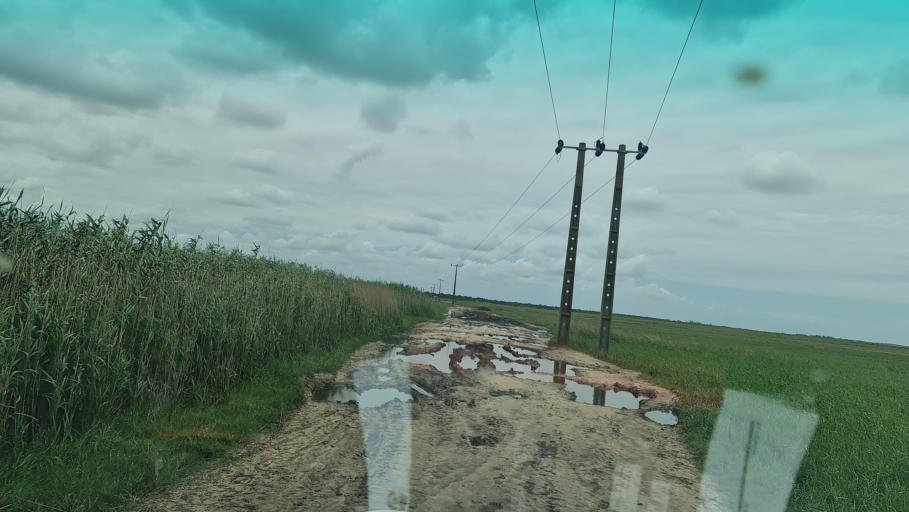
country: MZ
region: Maputo City
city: Maputo
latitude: -25.7154
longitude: 32.7021
